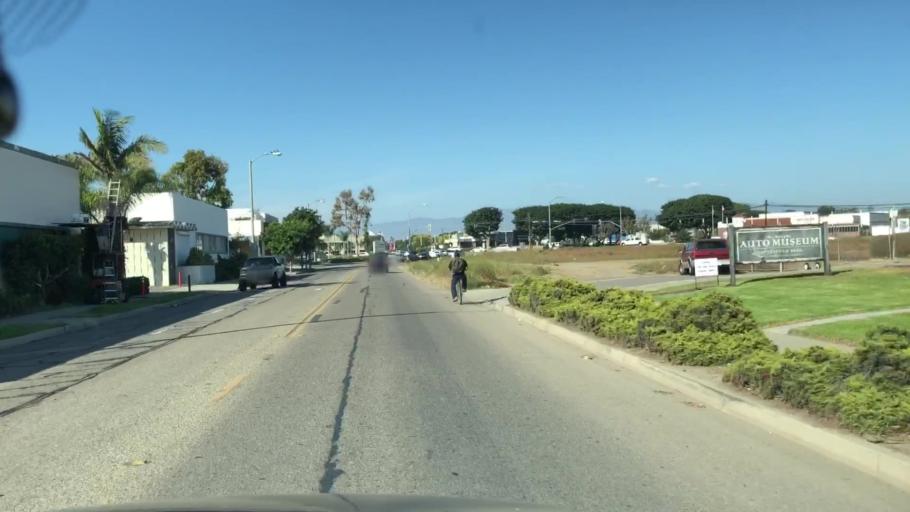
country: US
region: California
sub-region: Ventura County
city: Oxnard
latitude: 34.1782
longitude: -119.1656
